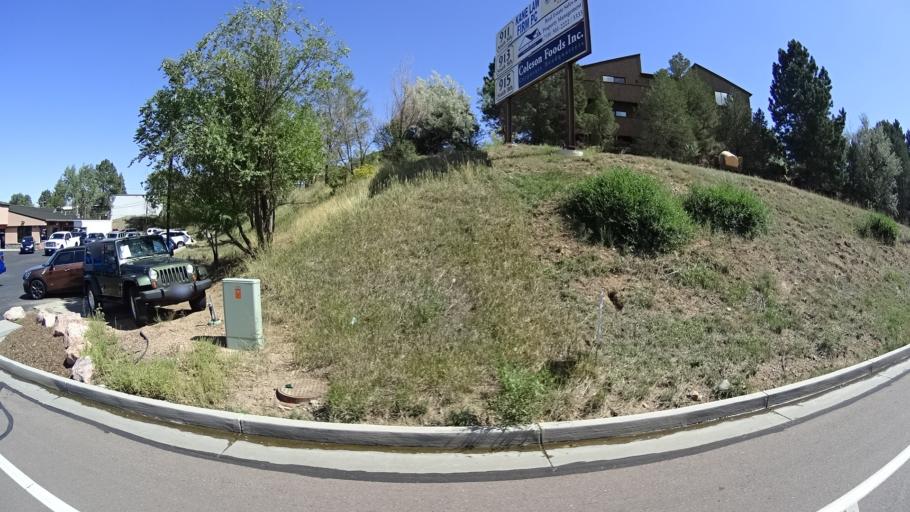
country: US
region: Colorado
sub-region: El Paso County
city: Colorado Springs
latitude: 38.8209
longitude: -104.8414
